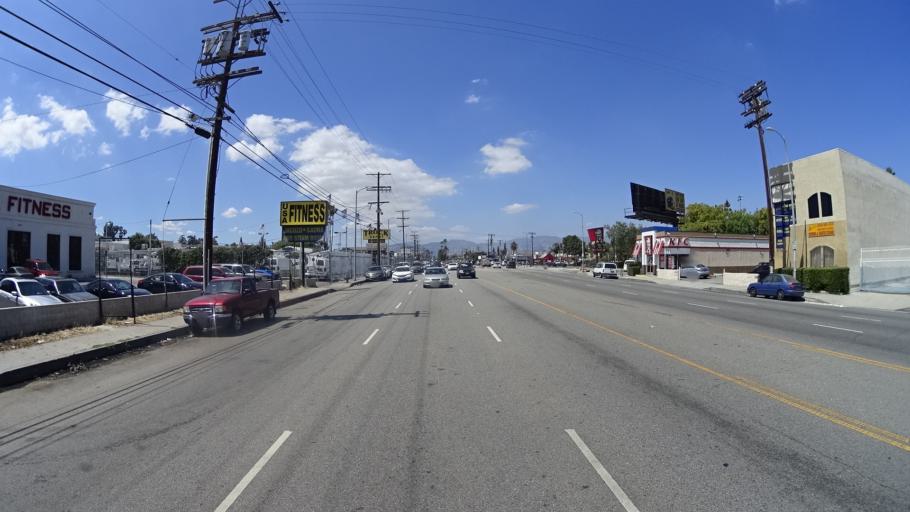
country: US
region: California
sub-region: Los Angeles County
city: Van Nuys
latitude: 34.2296
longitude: -118.4677
